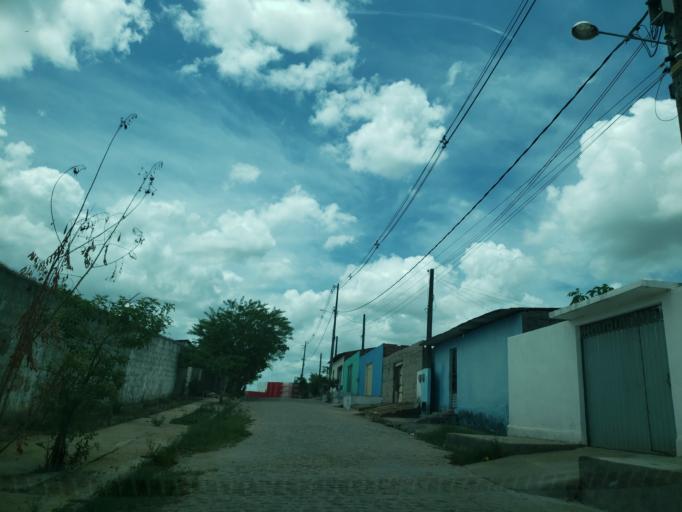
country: BR
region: Alagoas
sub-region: Uniao Dos Palmares
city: Uniao dos Palmares
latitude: -9.1508
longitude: -36.0123
